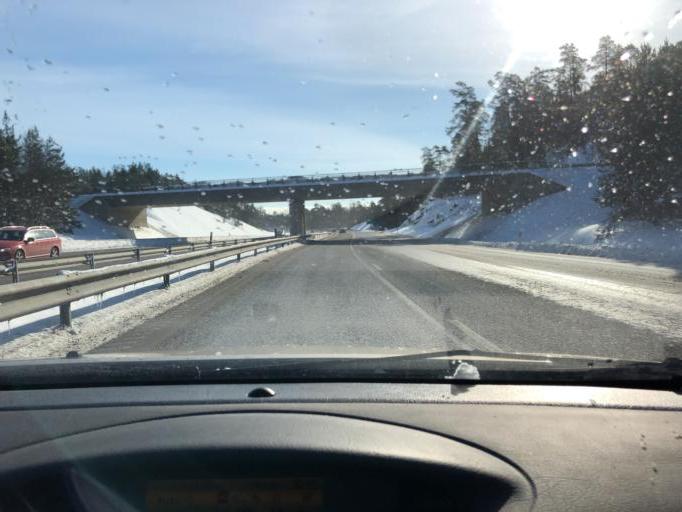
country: SE
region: Stockholm
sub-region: Nacka Kommun
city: Boo
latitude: 59.3271
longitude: 18.3301
